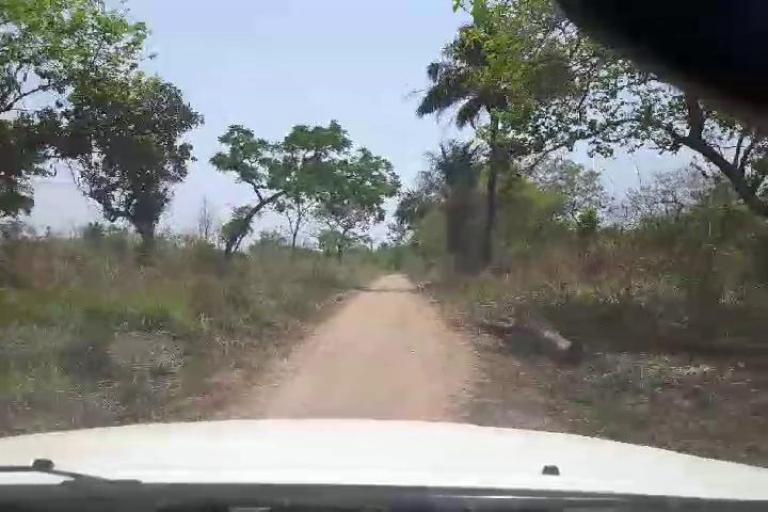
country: SL
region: Northern Province
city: Alikalia
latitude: 9.0735
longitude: -11.4786
